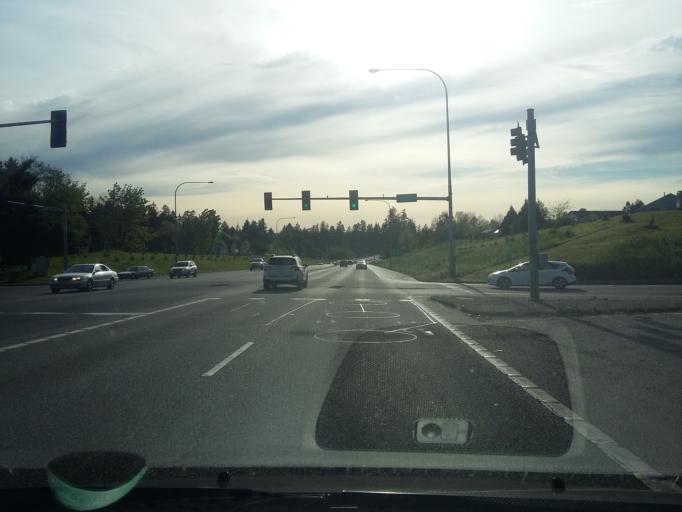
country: US
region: Washington
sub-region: Clark County
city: Minnehaha
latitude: 45.6472
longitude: -122.6282
